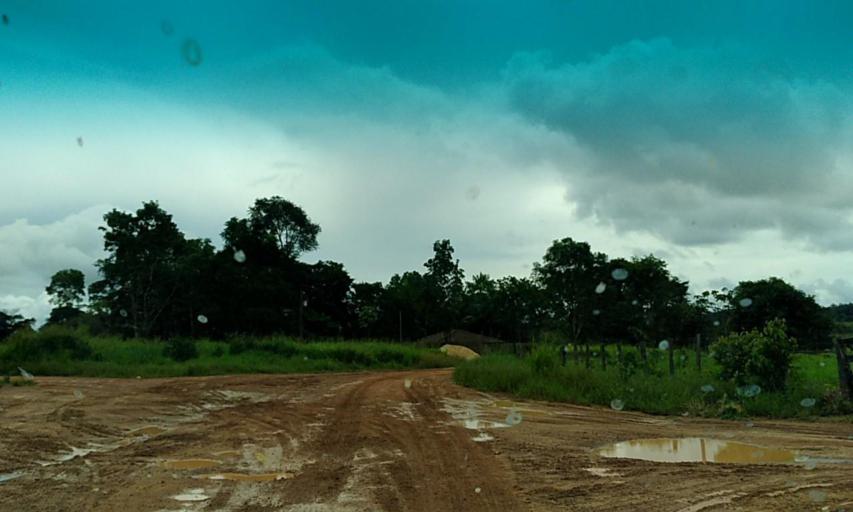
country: BR
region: Para
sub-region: Altamira
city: Altamira
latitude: -3.0780
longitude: -51.7037
